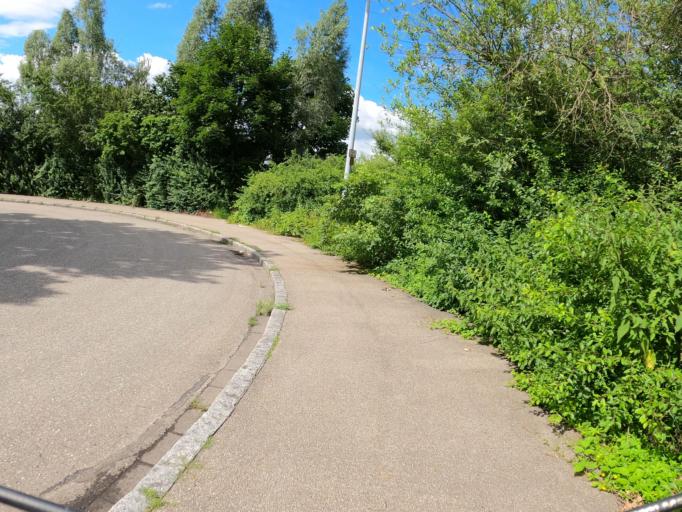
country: DE
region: Bavaria
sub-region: Swabia
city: Neu-Ulm
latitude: 48.3916
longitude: 10.0455
